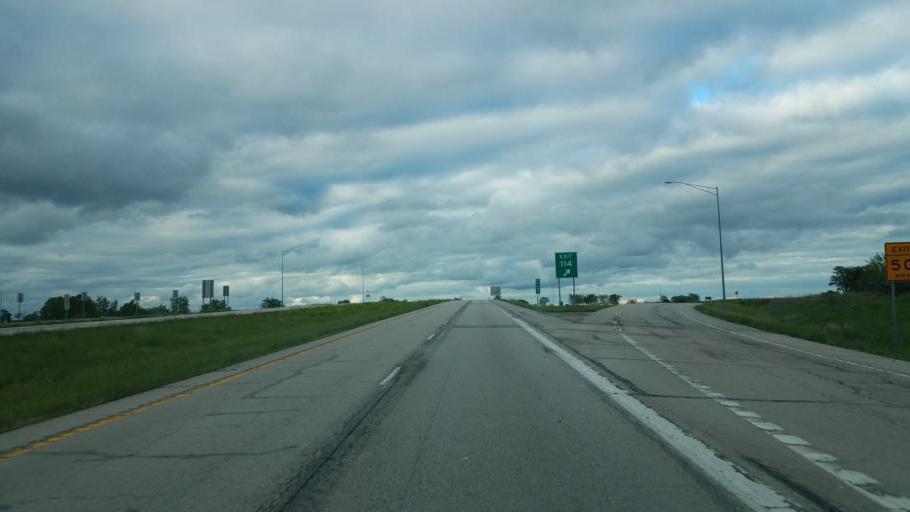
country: US
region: Iowa
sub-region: Decatur County
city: Lamoni
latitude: 40.5726
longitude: -93.9399
